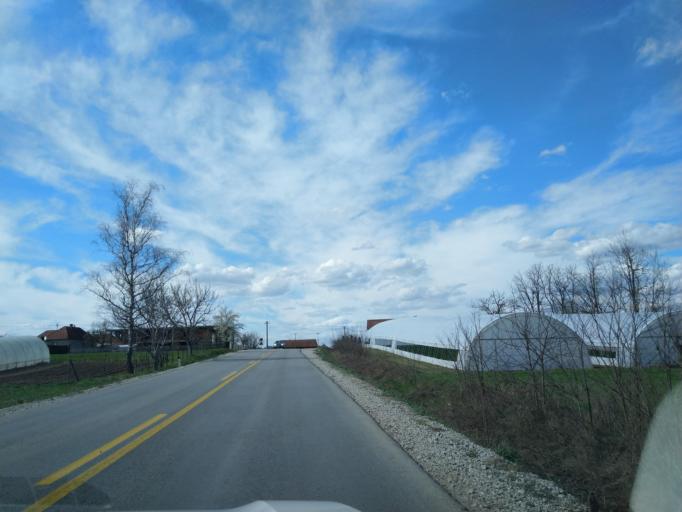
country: RS
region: Central Serbia
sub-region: Zlatiborski Okrug
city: Arilje
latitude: 43.7946
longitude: 20.0995
